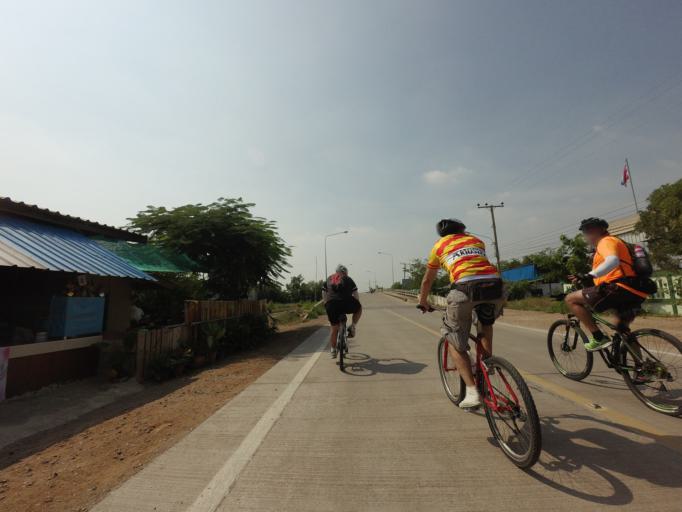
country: TH
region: Samut Sakhon
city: Samut Sakhon
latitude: 13.5131
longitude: 100.3876
